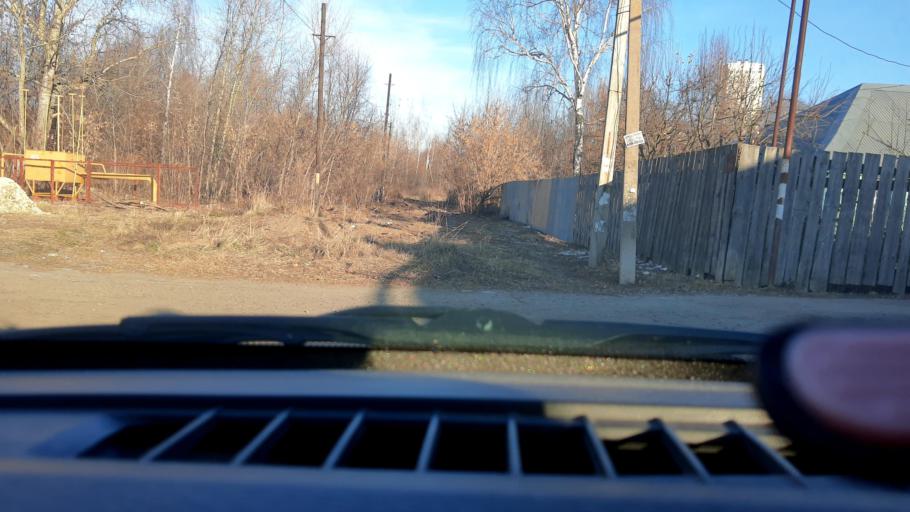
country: RU
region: Nizjnij Novgorod
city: Nizhniy Novgorod
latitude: 56.2993
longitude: 43.9184
